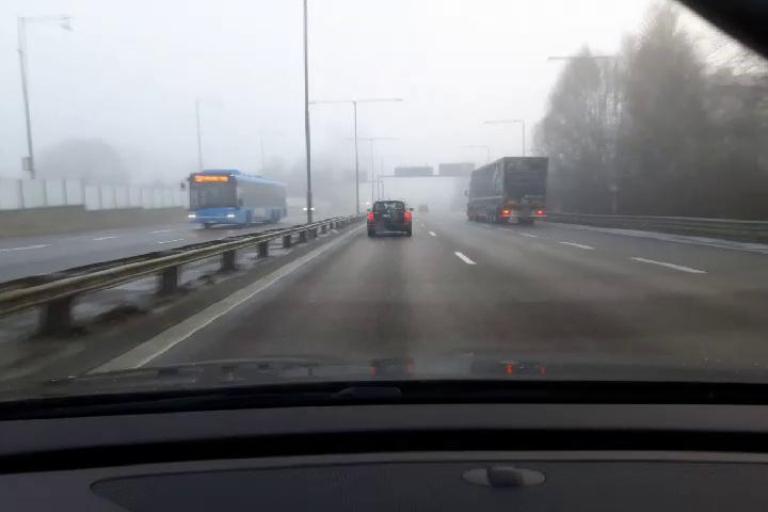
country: SE
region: Vaestra Goetaland
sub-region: Goteborg
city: Majorna
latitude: 57.6934
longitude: 11.9163
